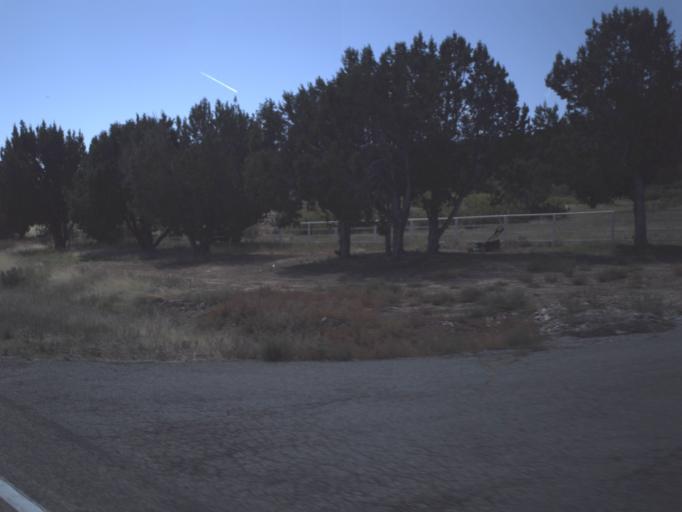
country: US
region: Utah
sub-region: Washington County
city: Enterprise
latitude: 37.5147
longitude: -113.6346
